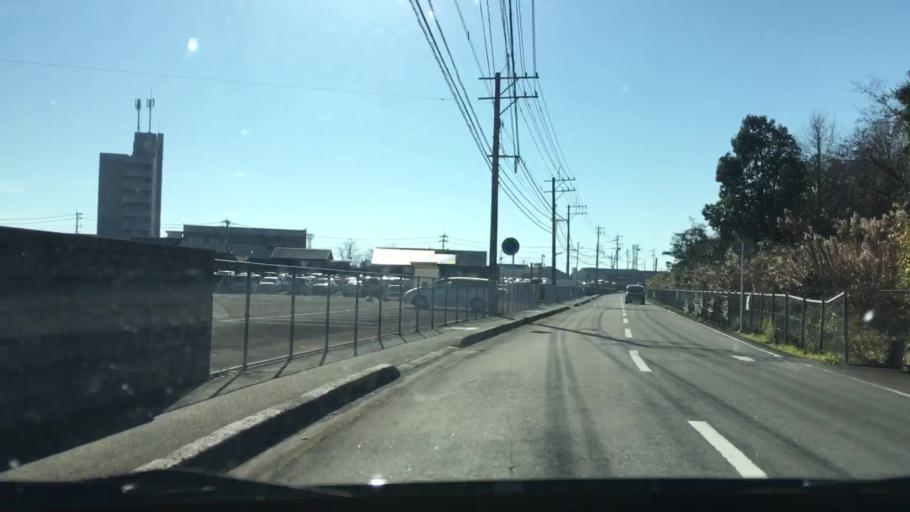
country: JP
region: Kagoshima
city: Kajiki
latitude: 31.7965
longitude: 130.7156
